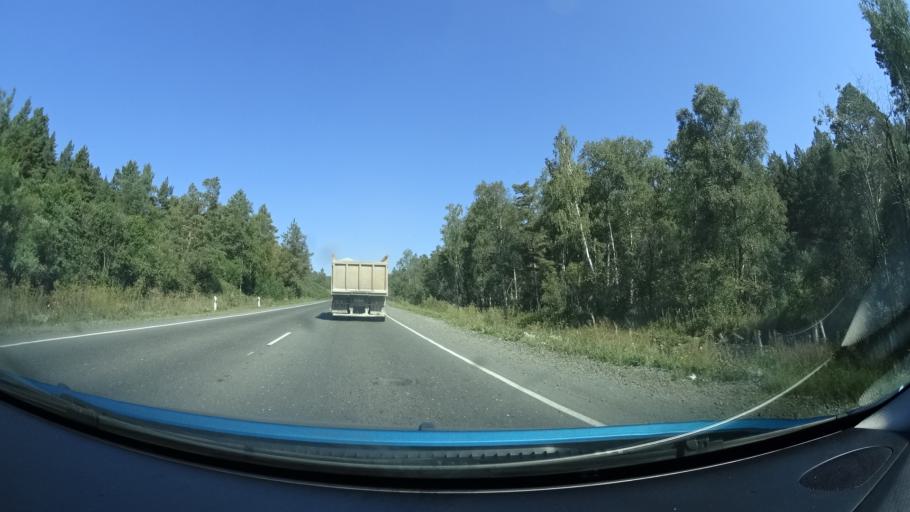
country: RU
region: Bashkortostan
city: Abzakovo
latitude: 53.8695
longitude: 58.5382
